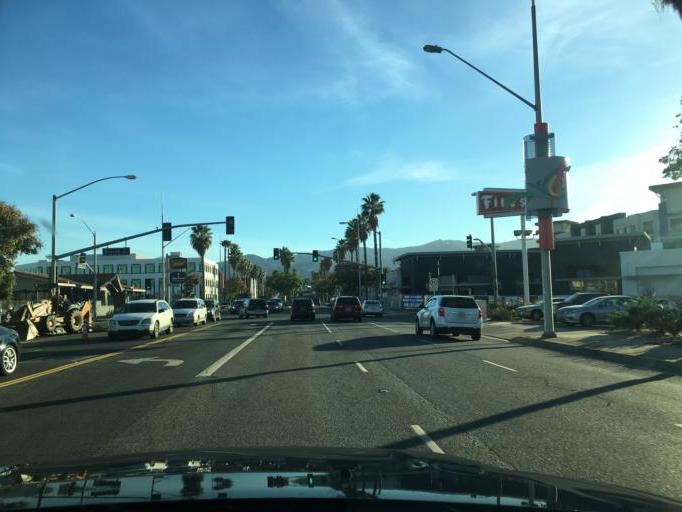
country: US
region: California
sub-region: Riverside County
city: Corona
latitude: 33.8884
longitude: -117.5643
